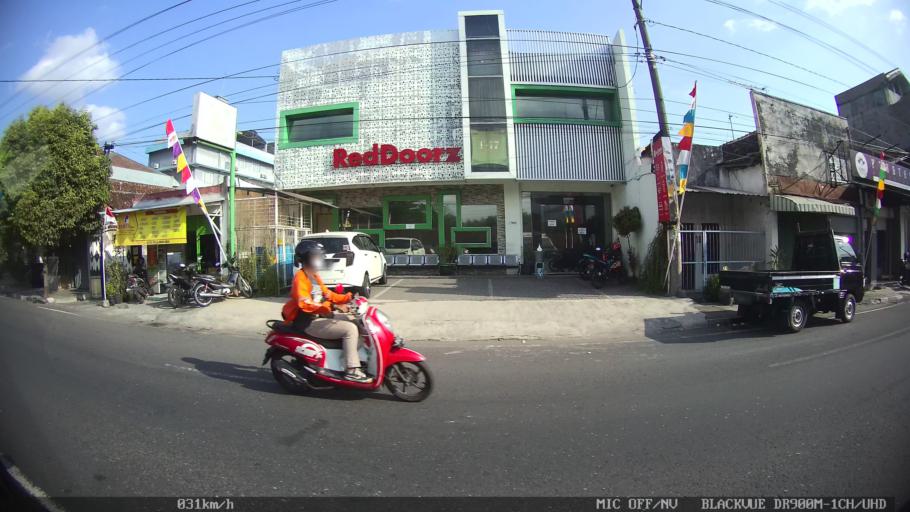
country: ID
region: Daerah Istimewa Yogyakarta
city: Yogyakarta
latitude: -7.8014
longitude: 110.3488
